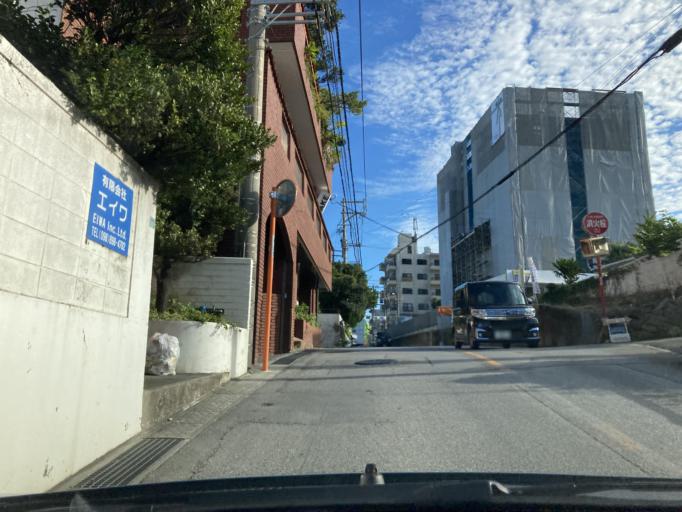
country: JP
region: Okinawa
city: Ginowan
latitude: 26.2774
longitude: 127.7457
